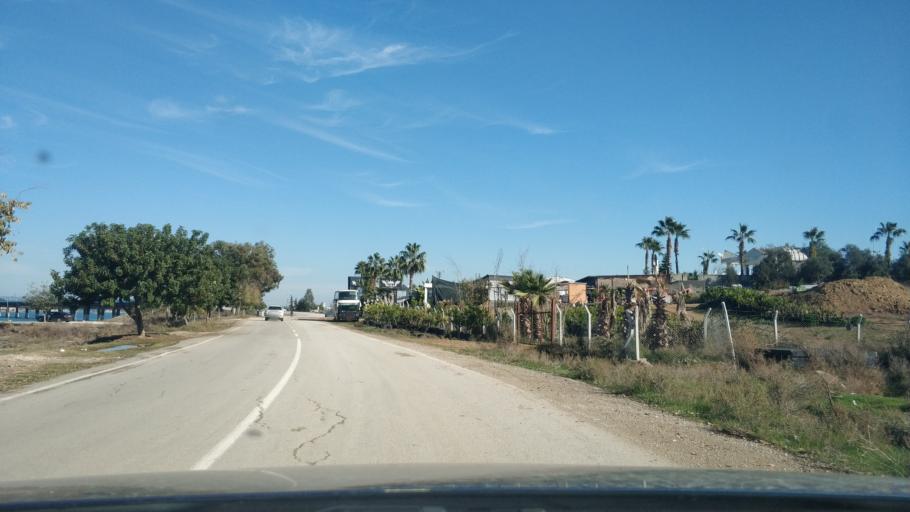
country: TR
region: Adana
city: Seyhan
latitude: 37.0685
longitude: 35.2681
